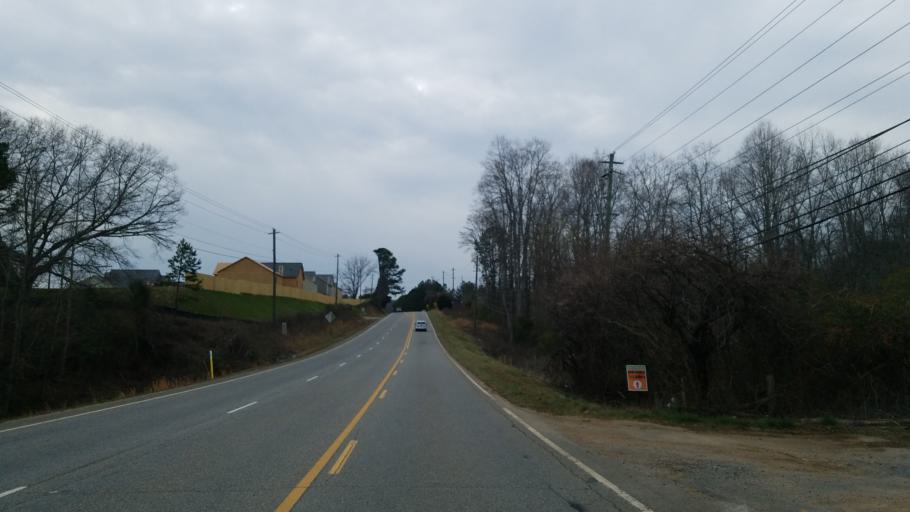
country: US
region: Georgia
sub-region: Cherokee County
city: Ball Ground
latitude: 34.2885
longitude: -84.4269
